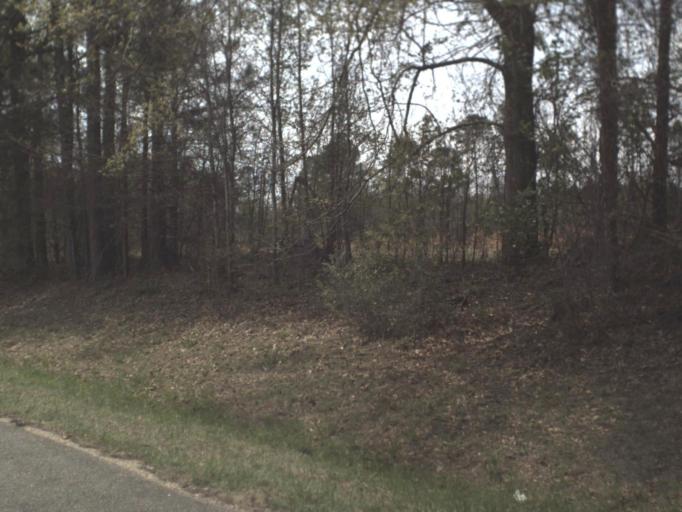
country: US
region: Florida
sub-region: Jackson County
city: Graceville
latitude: 30.9050
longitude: -85.5222
